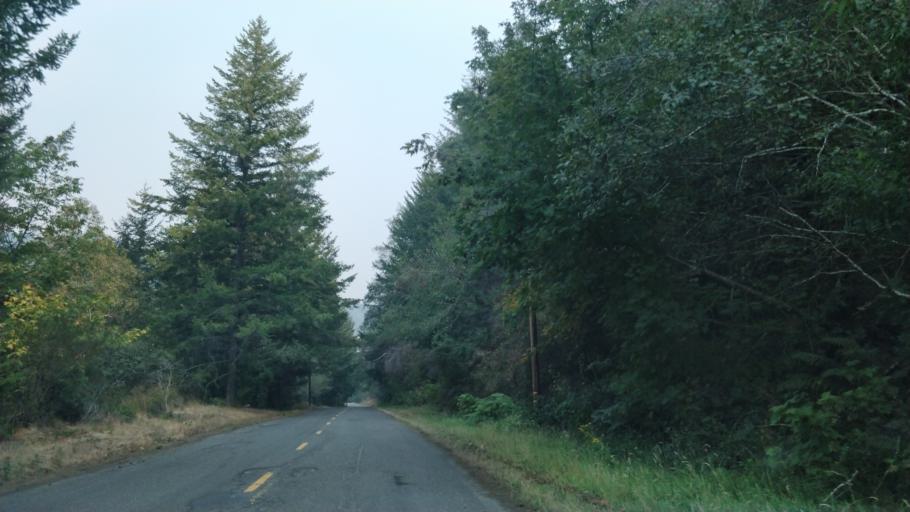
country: US
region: California
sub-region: Humboldt County
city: Rio Dell
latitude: 40.3107
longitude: -124.2739
